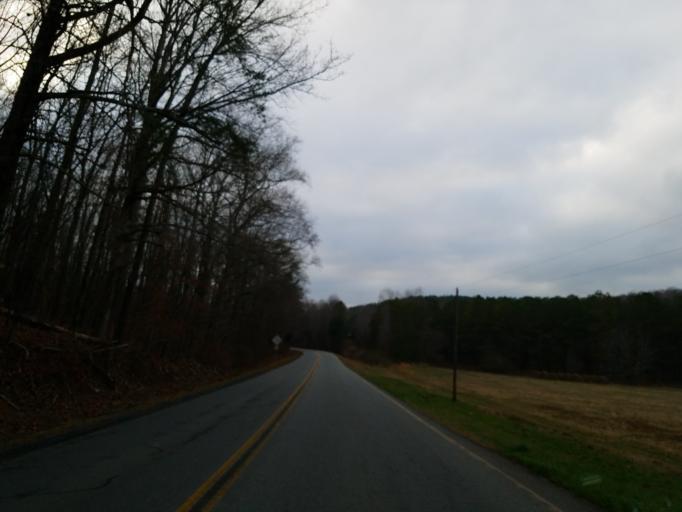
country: US
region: Georgia
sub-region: Bartow County
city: Rydal
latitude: 34.3495
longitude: -84.6738
